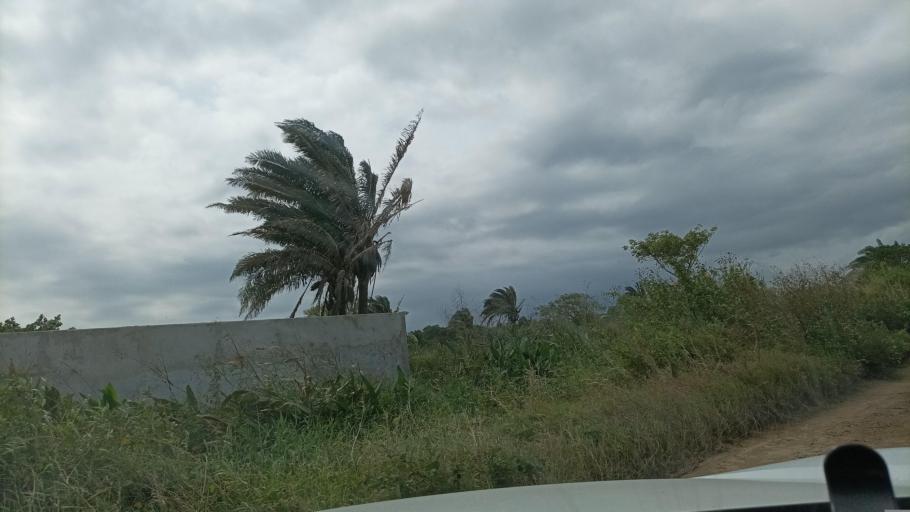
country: MX
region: Veracruz
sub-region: Coatzacoalcos
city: Fraccionamiento Ciudad Olmeca
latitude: 18.1785
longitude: -94.5914
